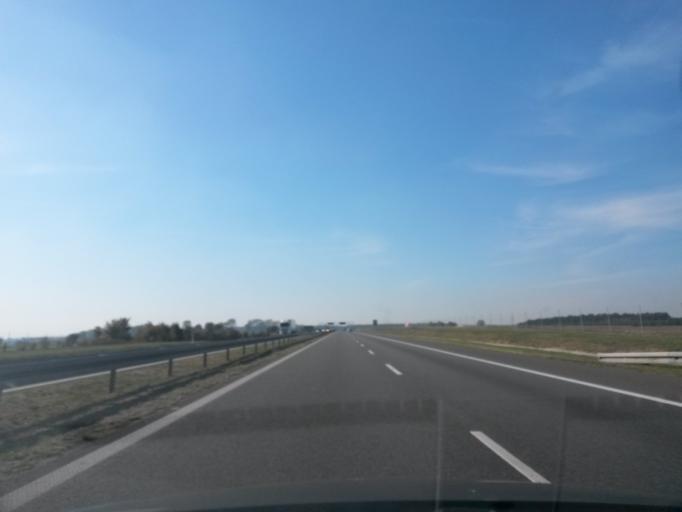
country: PL
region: Opole Voivodeship
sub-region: Powiat strzelecki
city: Ujazd
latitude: 50.4476
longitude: 18.3377
